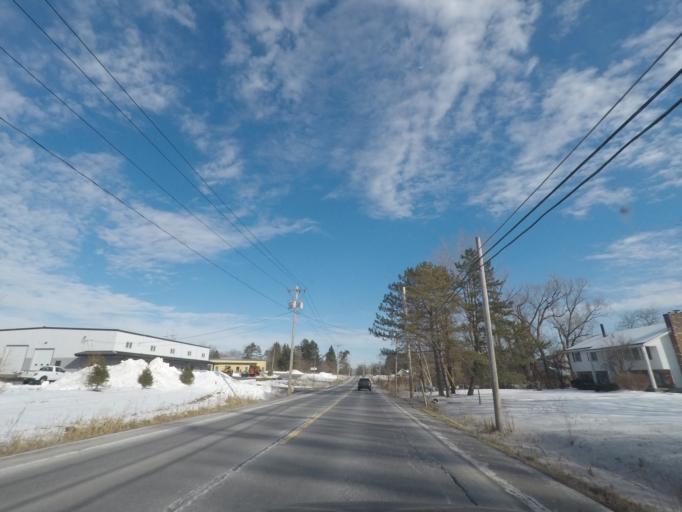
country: US
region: New York
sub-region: Schenectady County
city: Rotterdam
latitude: 42.7781
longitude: -74.0443
